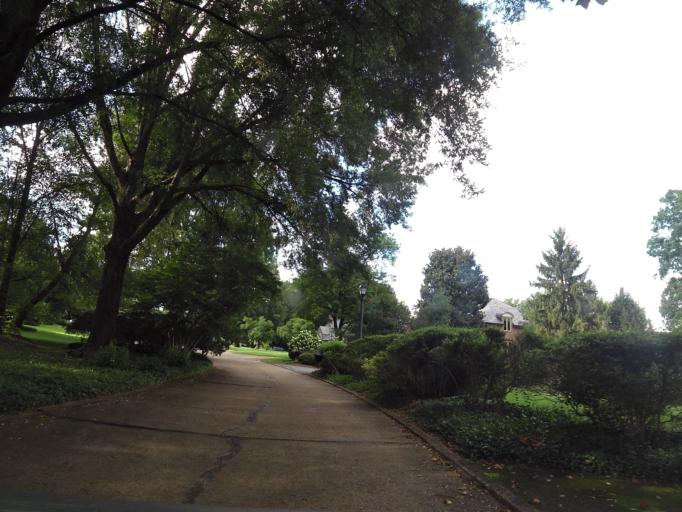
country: US
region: Tennessee
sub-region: Knox County
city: Knoxville
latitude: 35.9400
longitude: -83.9581
